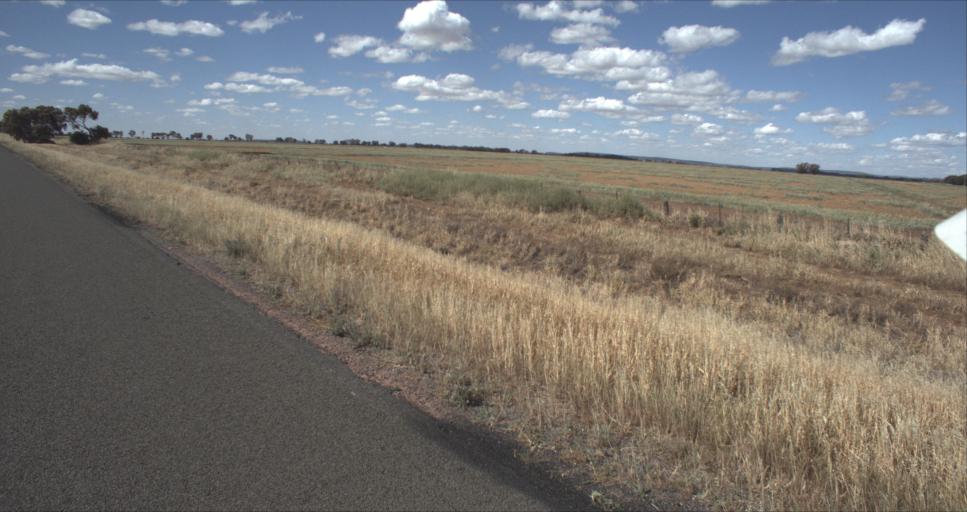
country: AU
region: New South Wales
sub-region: Leeton
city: Leeton
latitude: -34.4696
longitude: 146.2512
